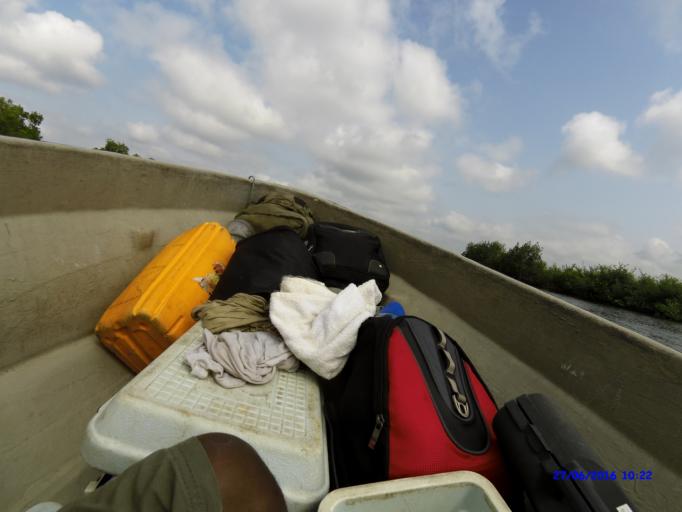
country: BJ
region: Mono
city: Come
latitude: 6.3678
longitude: 1.9308
